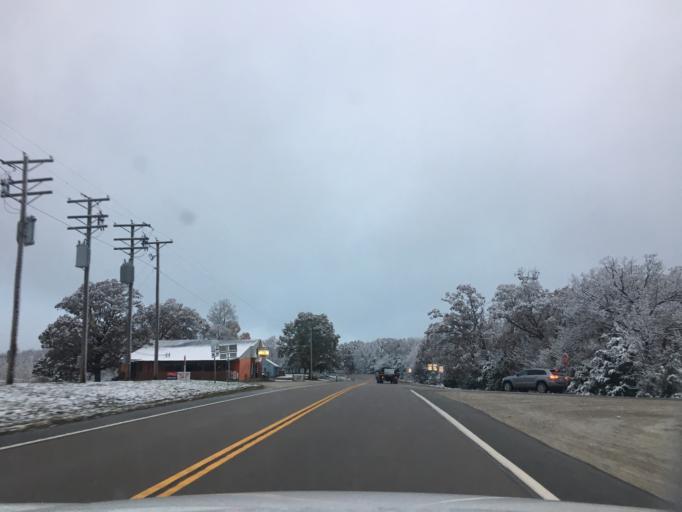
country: US
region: Missouri
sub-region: Osage County
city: Linn
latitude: 38.4741
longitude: -91.7840
